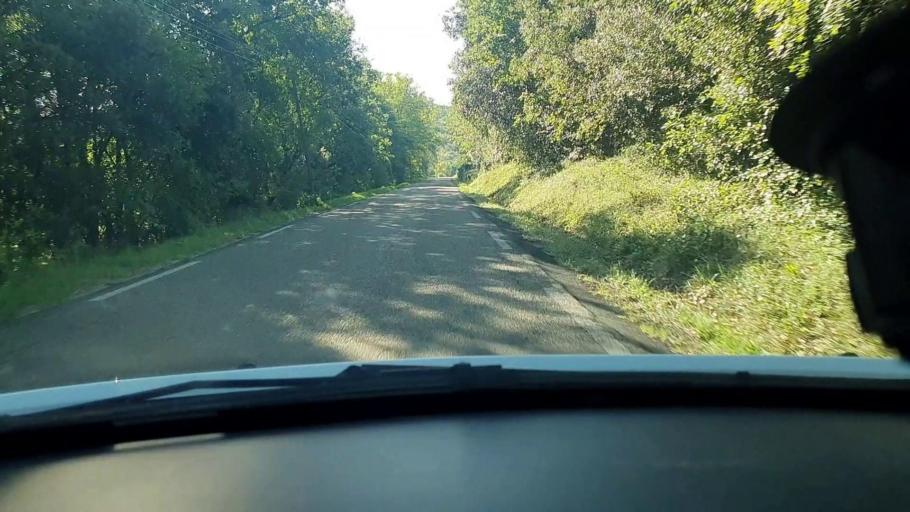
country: FR
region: Languedoc-Roussillon
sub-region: Departement du Gard
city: Goudargues
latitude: 44.1953
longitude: 4.4781
